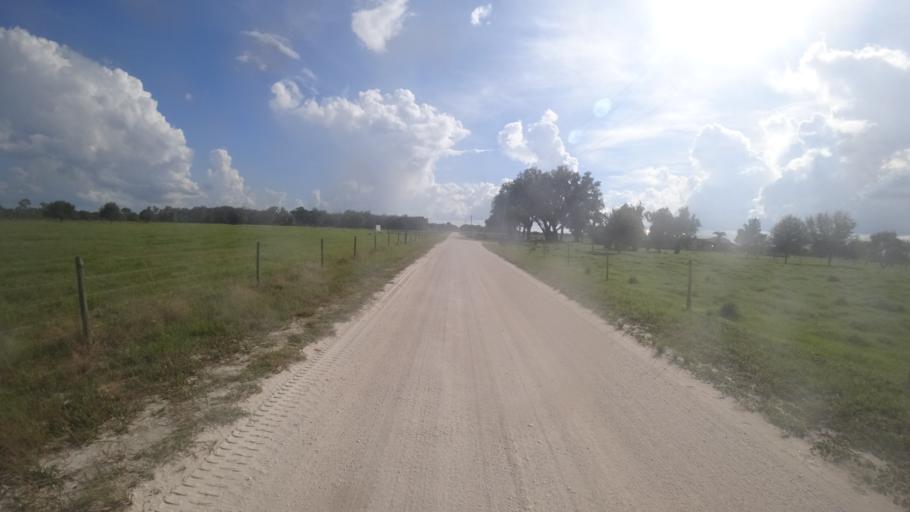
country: US
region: Florida
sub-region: Hillsborough County
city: Balm
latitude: 27.6390
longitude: -82.1239
